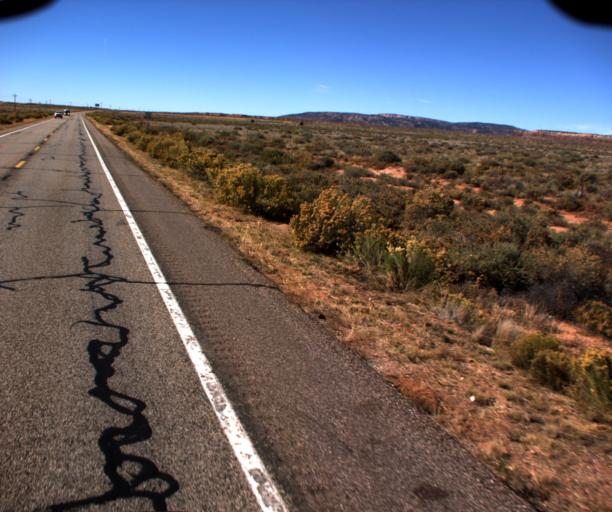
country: US
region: Arizona
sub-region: Coconino County
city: Fredonia
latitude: 36.8840
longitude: -112.6353
